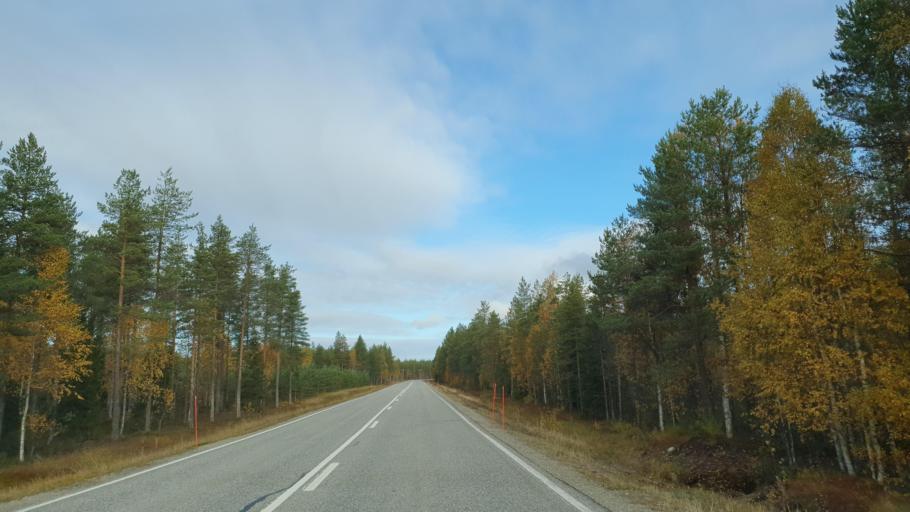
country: FI
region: Kainuu
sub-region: Kehys-Kainuu
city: Puolanka
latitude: 65.3058
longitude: 27.4687
